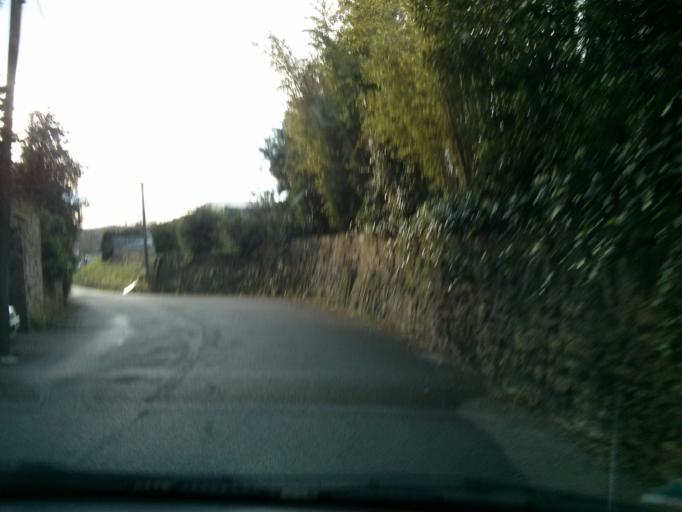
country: FR
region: Languedoc-Roussillon
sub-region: Departement du Gard
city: Aigues-Vives
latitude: 43.7368
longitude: 4.1831
